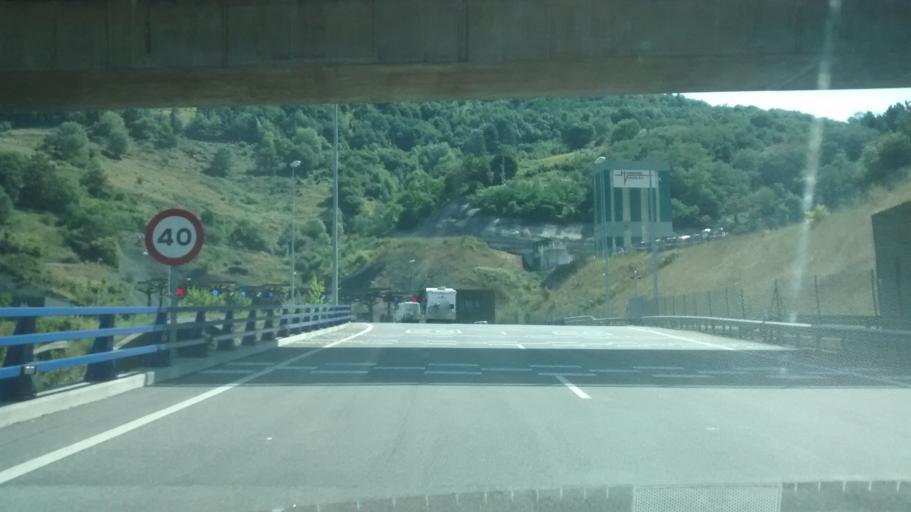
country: ES
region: Basque Country
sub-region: Bizkaia
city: Bilbao
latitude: 43.2372
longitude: -2.9459
